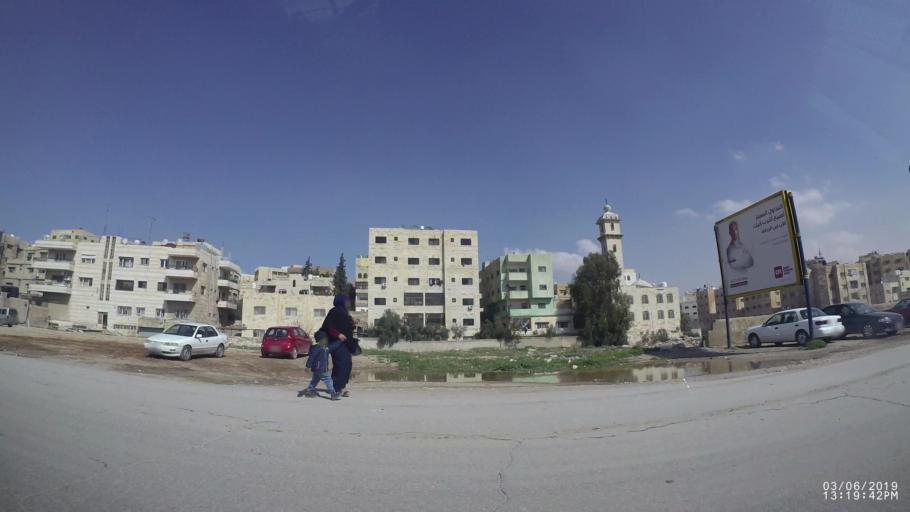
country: JO
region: Zarqa
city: Zarqa
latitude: 32.0437
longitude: 36.0940
